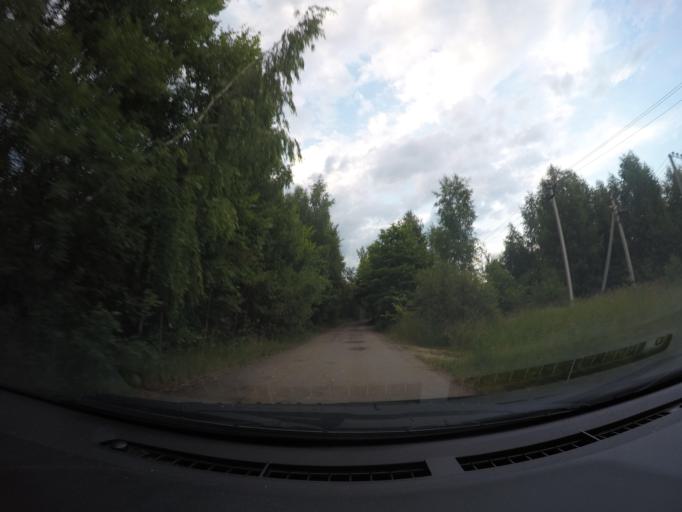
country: RU
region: Moskovskaya
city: Krasnyy Tkach
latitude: 55.4225
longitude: 39.2375
